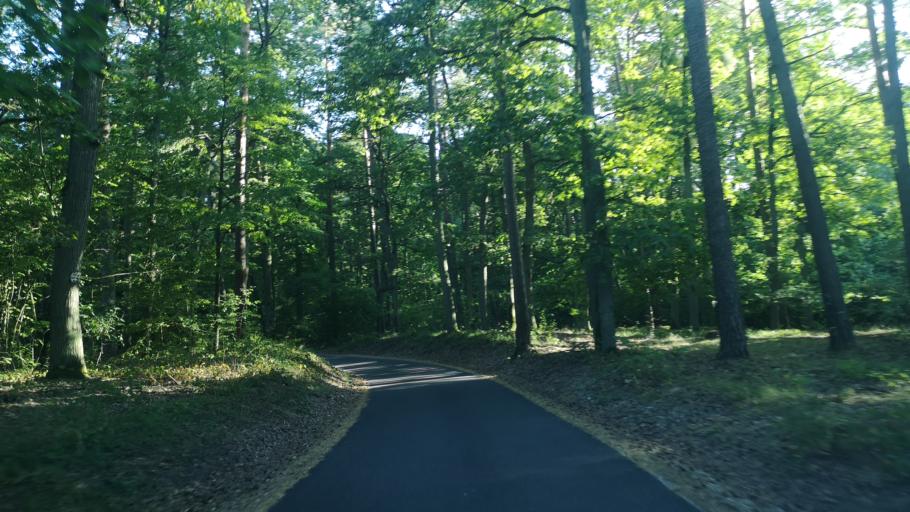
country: PL
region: Kujawsko-Pomorskie
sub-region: Powiat swiecki
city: Warlubie
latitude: 53.4777
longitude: 18.6318
